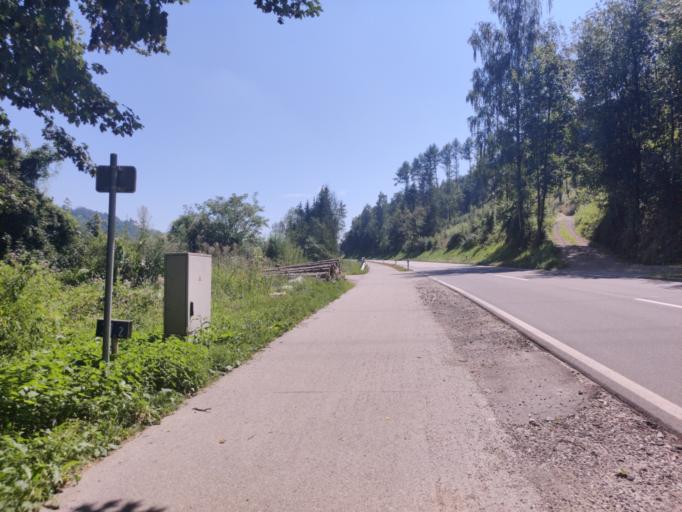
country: AT
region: Upper Austria
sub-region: Politischer Bezirk Rohrbach
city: Pfarrkirchen im Muehlkreis
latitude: 48.4875
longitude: 13.7472
